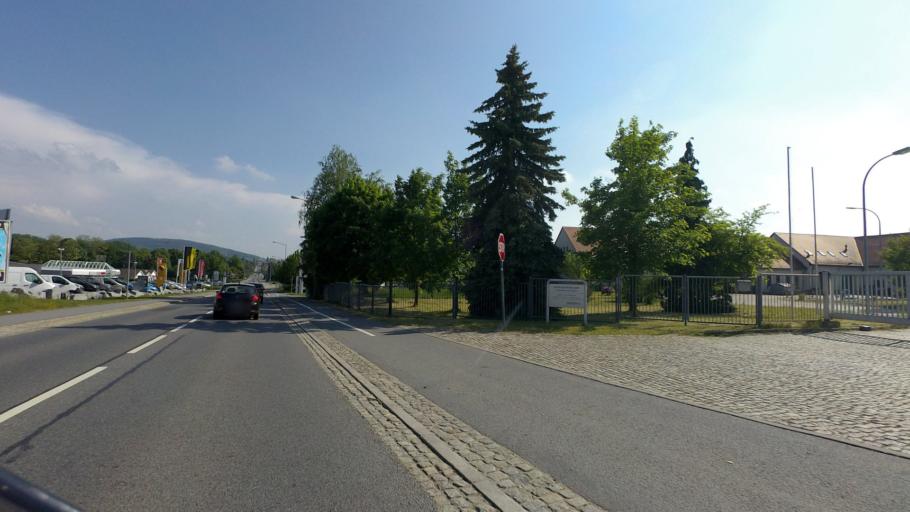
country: DE
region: Saxony
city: Bautzen
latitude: 51.1657
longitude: 14.4272
